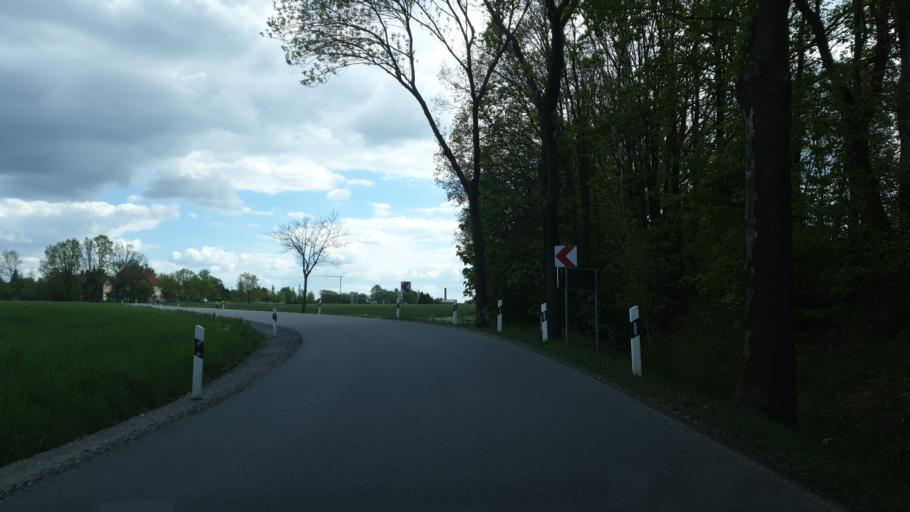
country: DE
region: Saxony
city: Niederdorf
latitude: 50.7660
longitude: 12.7755
